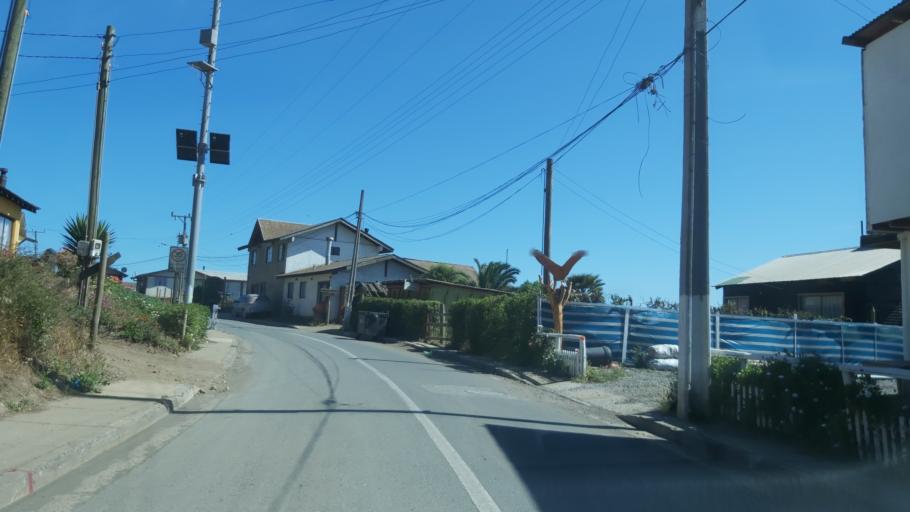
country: CL
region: Maule
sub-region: Provincia de Talca
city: Constitucion
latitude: -34.7553
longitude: -72.0837
